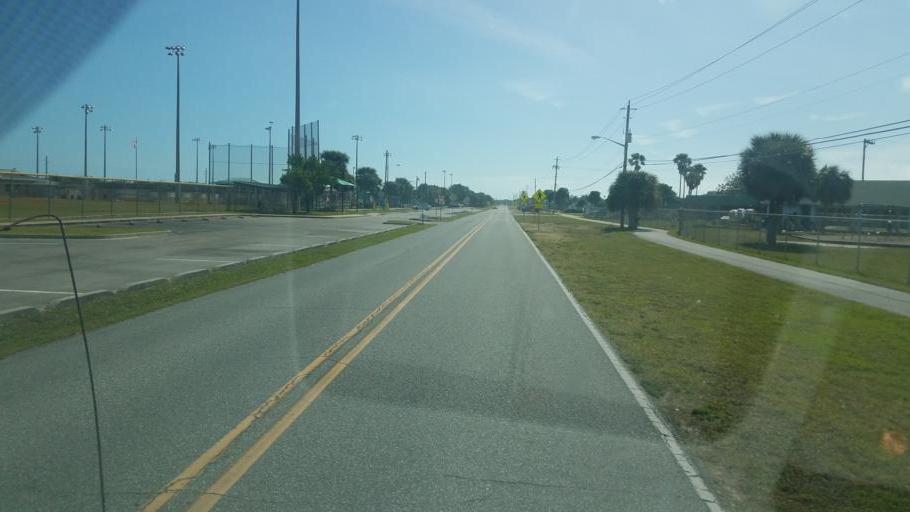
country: US
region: Florida
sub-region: Brevard County
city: Melbourne Beach
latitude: 28.0557
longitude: -80.5559
